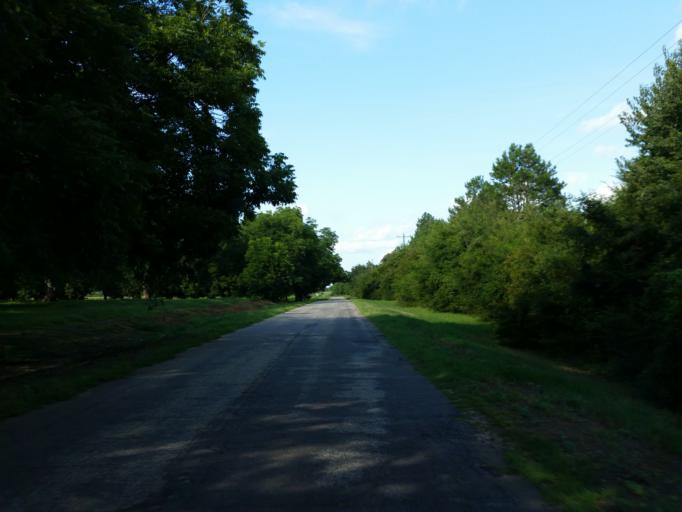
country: US
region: Georgia
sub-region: Lee County
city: Leesburg
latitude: 31.9143
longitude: -84.0166
